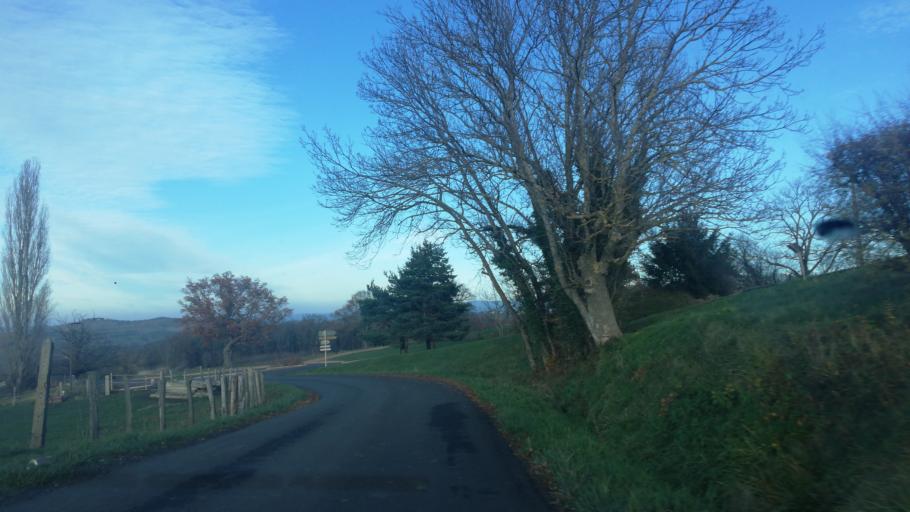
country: FR
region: Auvergne
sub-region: Departement du Puy-de-Dome
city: Billom
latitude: 45.6986
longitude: 3.3565
